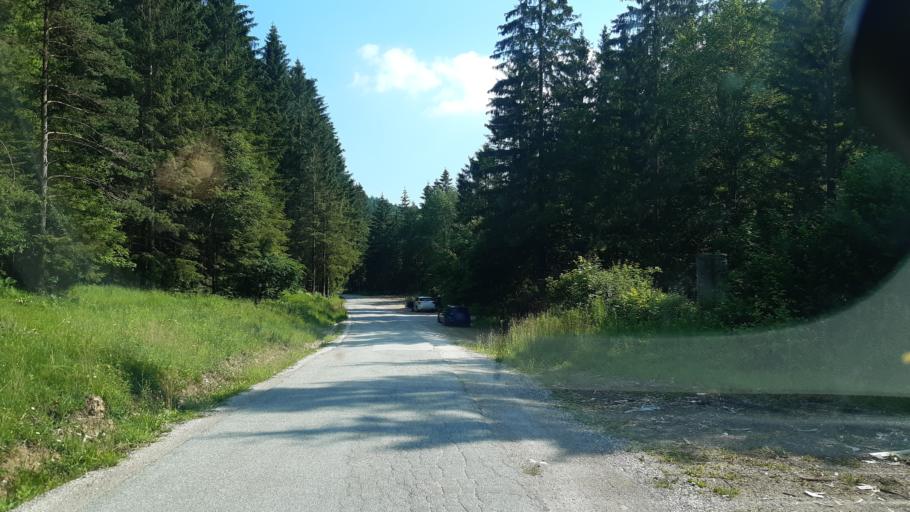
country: SI
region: Radovljica
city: Radovljica
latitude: 46.3867
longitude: 14.2176
